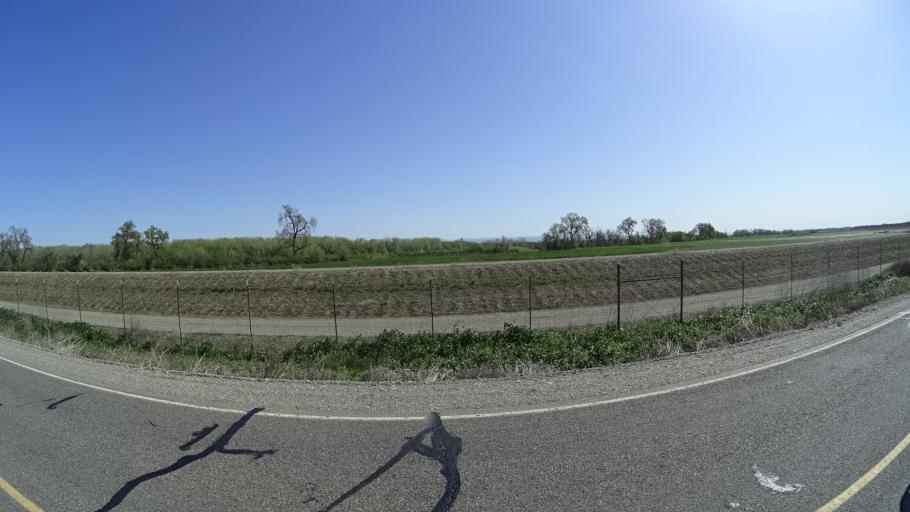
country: US
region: California
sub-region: Glenn County
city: Hamilton City
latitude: 39.7628
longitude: -122.0286
